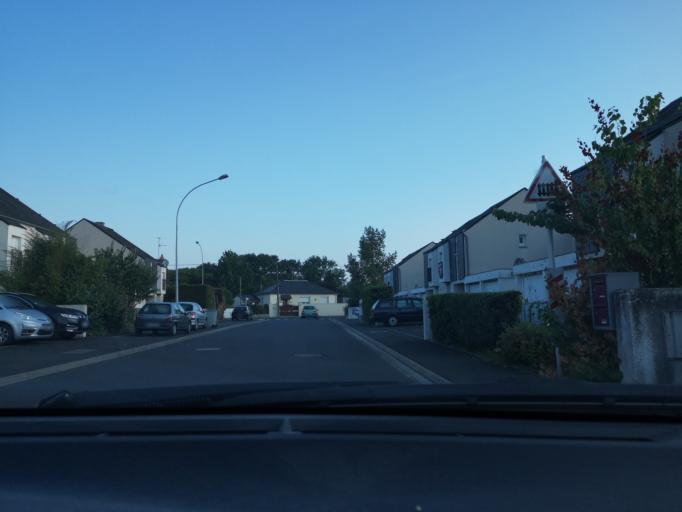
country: FR
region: Centre
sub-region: Departement du Loiret
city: Fleury-les-Aubrais
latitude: 47.9410
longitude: 1.9267
